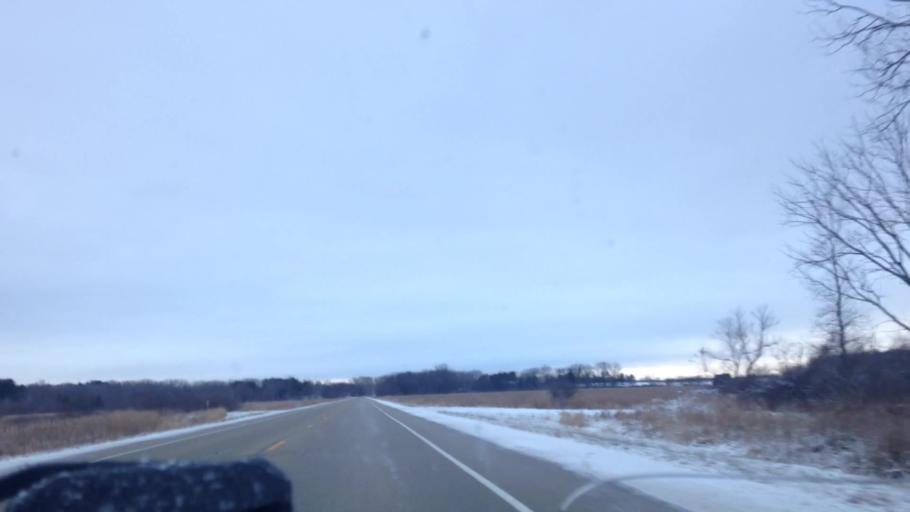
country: US
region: Wisconsin
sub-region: Dodge County
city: Horicon
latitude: 43.4665
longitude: -88.6089
